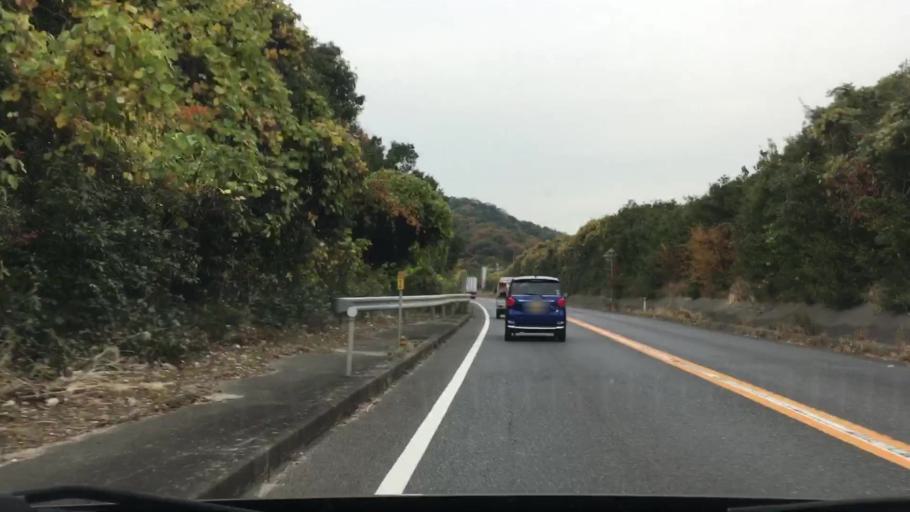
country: JP
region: Yamaguchi
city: Hofu
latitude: 34.0690
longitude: 131.6005
